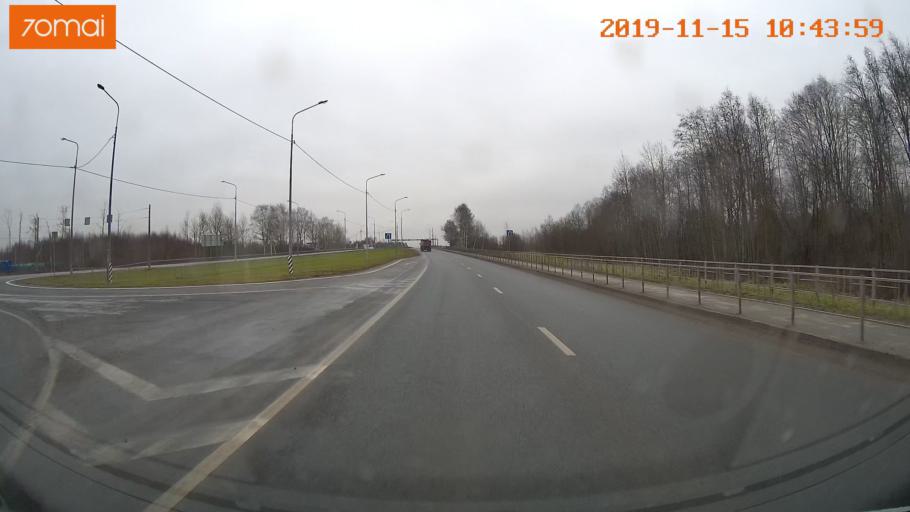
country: RU
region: Vologda
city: Sheksna
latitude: 59.2115
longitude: 38.5476
